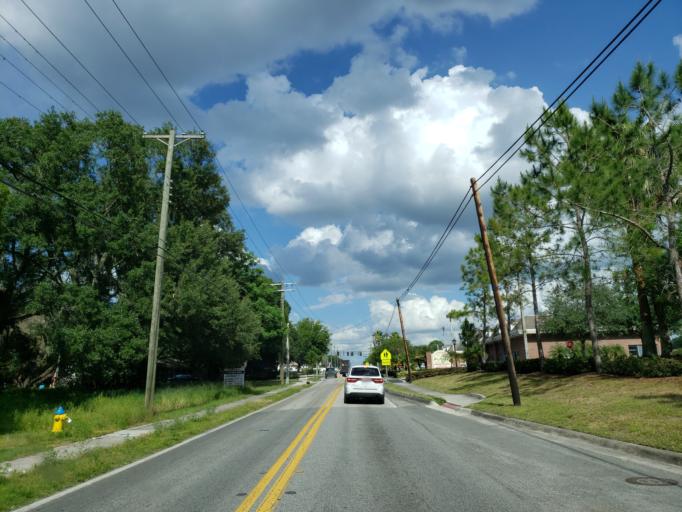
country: US
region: Florida
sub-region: Hillsborough County
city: Brandon
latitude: 27.9596
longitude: -82.2794
